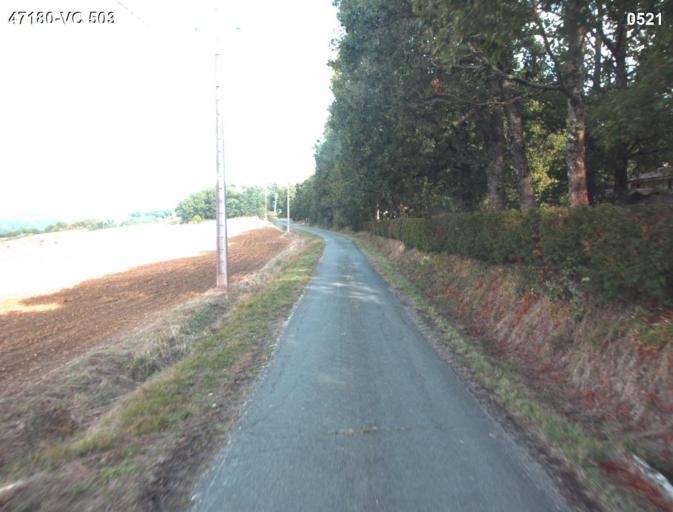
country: FR
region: Aquitaine
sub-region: Departement du Lot-et-Garonne
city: Port-Sainte-Marie
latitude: 44.1790
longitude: 0.4313
